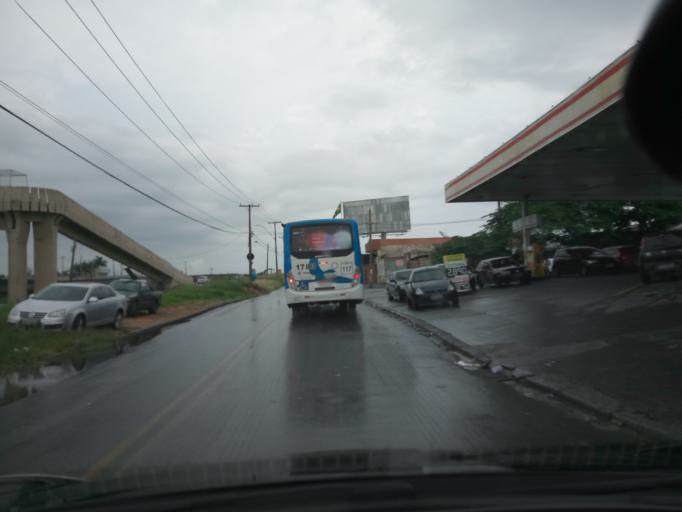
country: BR
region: Sao Paulo
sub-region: Campinas
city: Campinas
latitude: -22.9806
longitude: -47.1051
